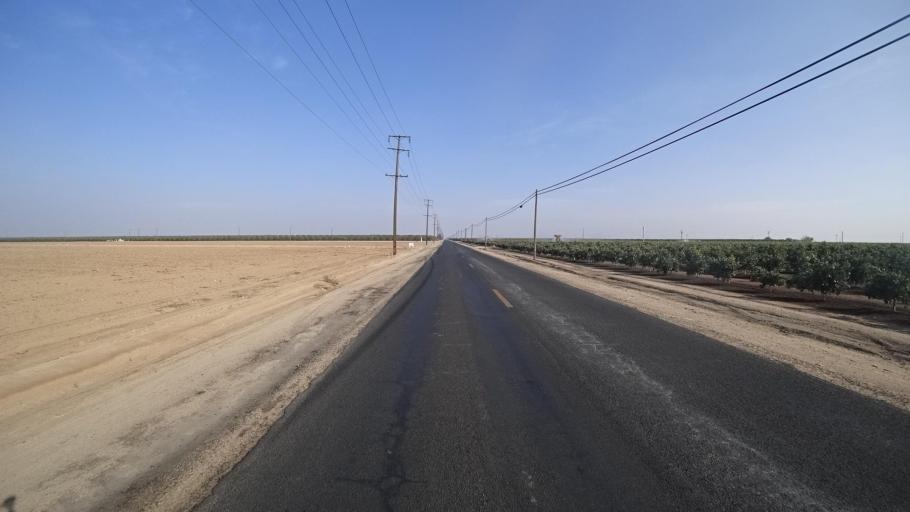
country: US
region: California
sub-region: Tulare County
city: Richgrove
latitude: 35.7761
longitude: -119.1551
